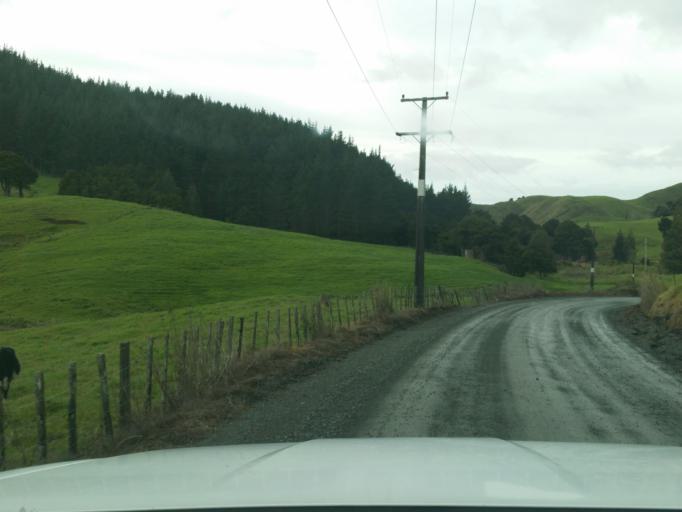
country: NZ
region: Northland
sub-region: Kaipara District
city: Dargaville
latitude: -35.8264
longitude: 173.8191
